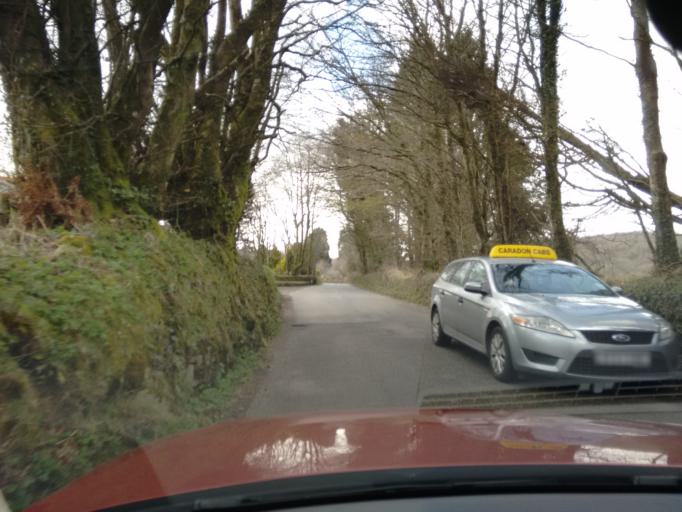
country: GB
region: England
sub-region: Cornwall
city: Liskeard
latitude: 50.4915
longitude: -4.4966
